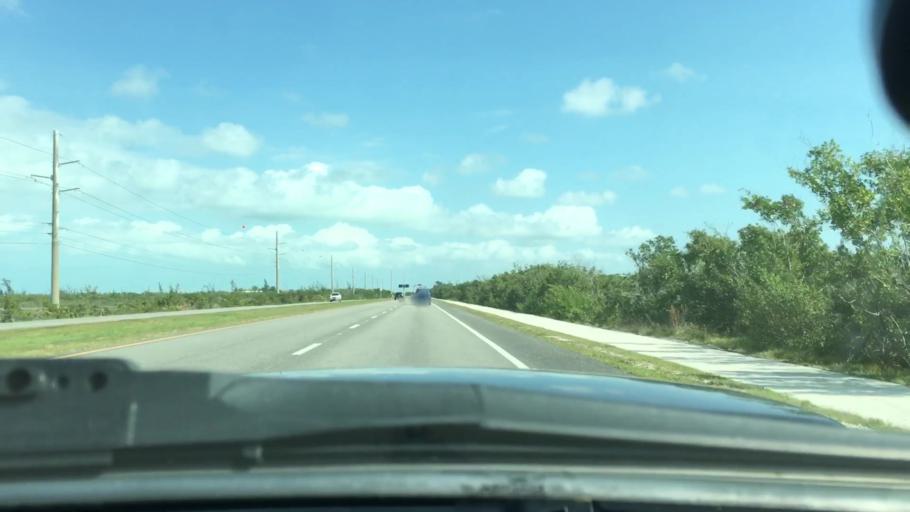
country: US
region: Florida
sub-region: Monroe County
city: Stock Island
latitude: 24.5825
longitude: -81.7026
